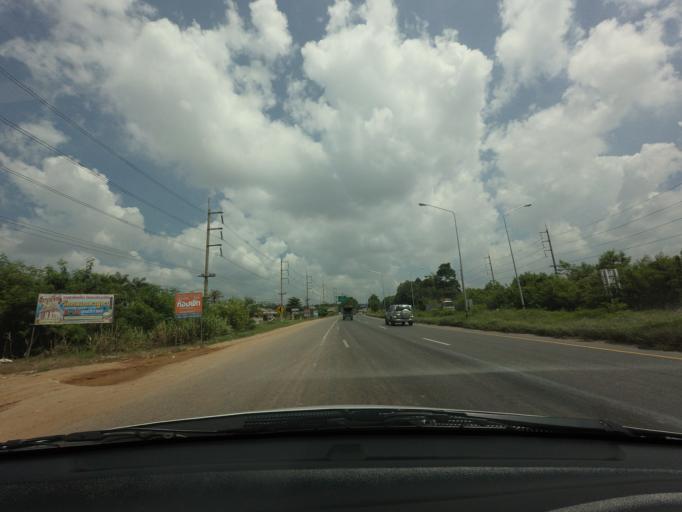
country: TH
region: Chachoengsao
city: Sanam Chai Khet
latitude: 13.7518
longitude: 101.4965
